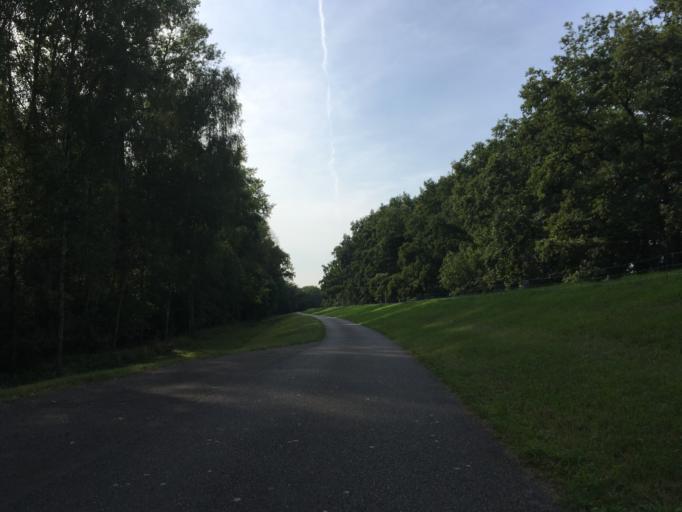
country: DE
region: Brandenburg
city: Brieskow-Finkenheerd
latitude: 52.2694
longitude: 14.6143
